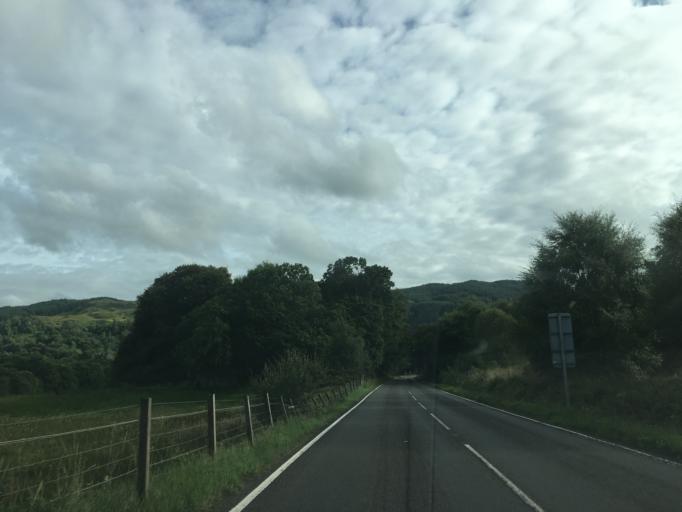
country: GB
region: Scotland
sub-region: Argyll and Bute
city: Oban
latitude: 56.3710
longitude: -5.4383
